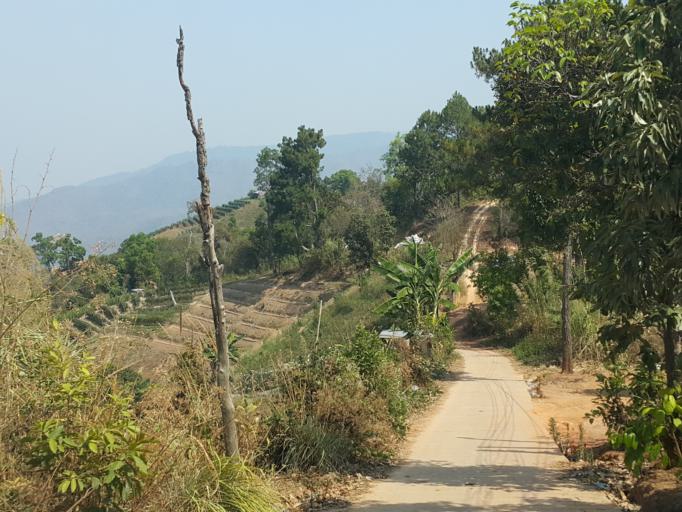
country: TH
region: Chiang Mai
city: Samoeng
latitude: 18.8857
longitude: 98.7893
